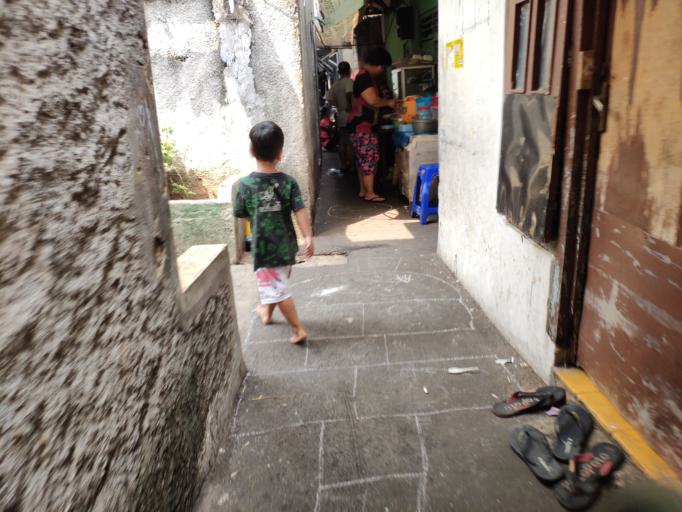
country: ID
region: Jakarta Raya
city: Jakarta
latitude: -6.1971
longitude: 106.8625
